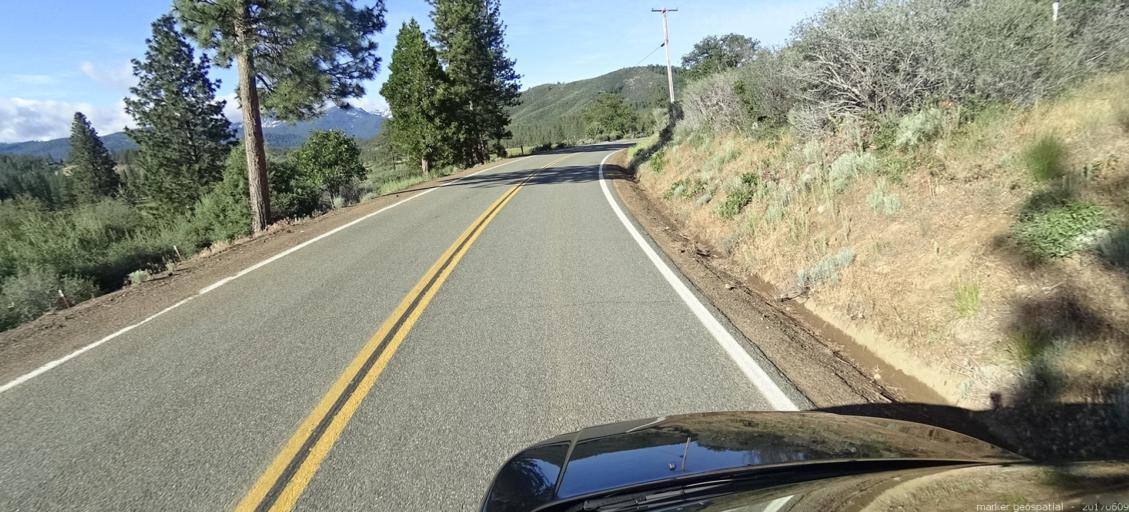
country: US
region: California
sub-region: Siskiyou County
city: Weed
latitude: 41.3581
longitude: -122.7197
